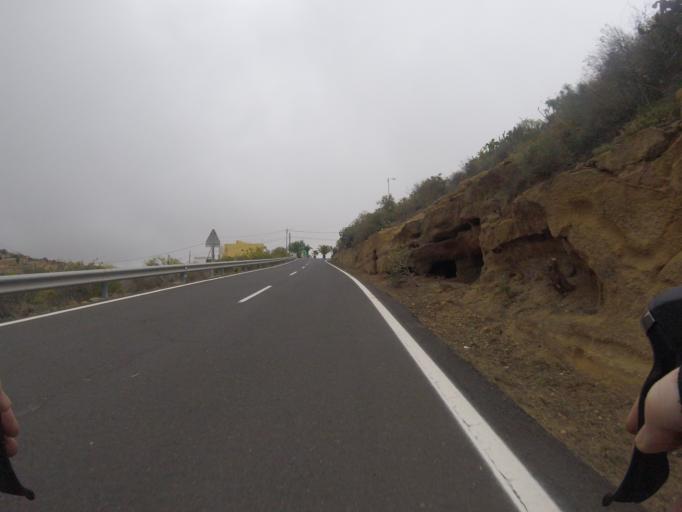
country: ES
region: Canary Islands
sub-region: Provincia de Santa Cruz de Tenerife
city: Lomo de Arico
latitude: 28.1974
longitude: -16.4715
